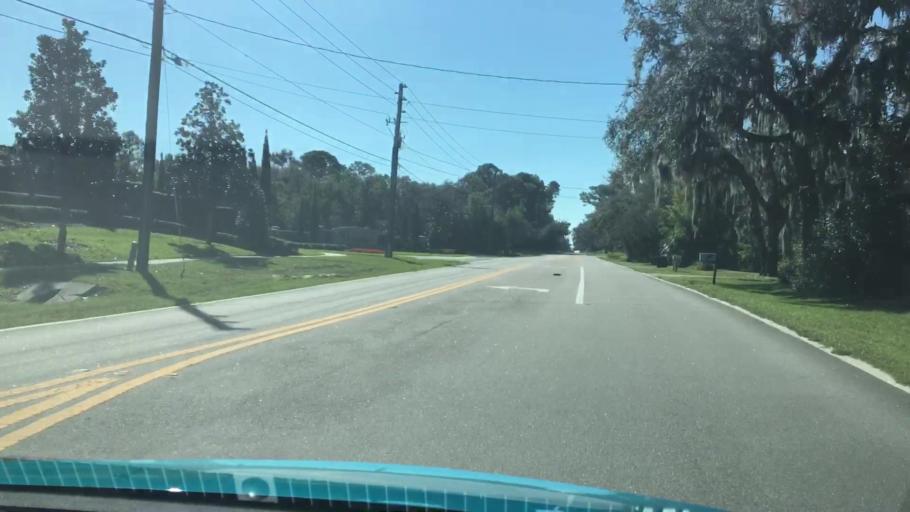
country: US
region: Florida
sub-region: Seminole County
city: Heathrow
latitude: 28.8175
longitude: -81.3631
